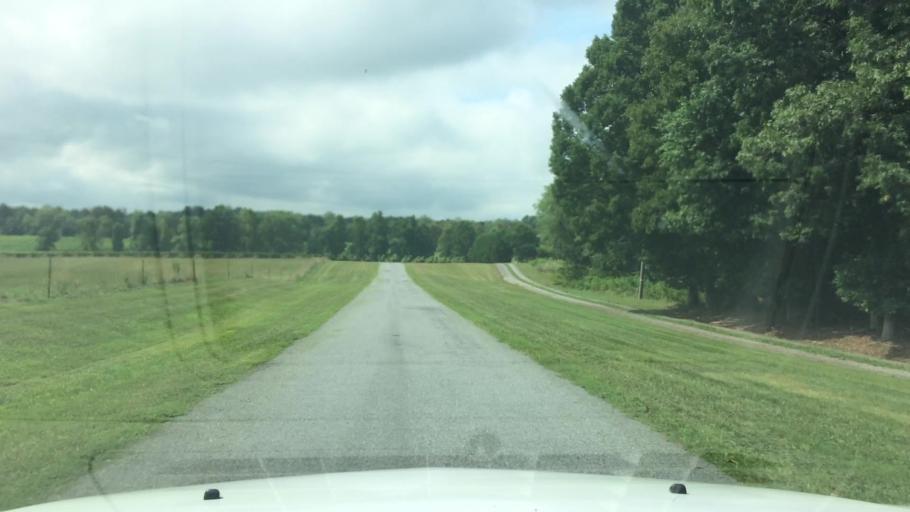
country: US
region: North Carolina
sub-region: Yadkin County
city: Jonesville
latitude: 36.0990
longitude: -80.8544
